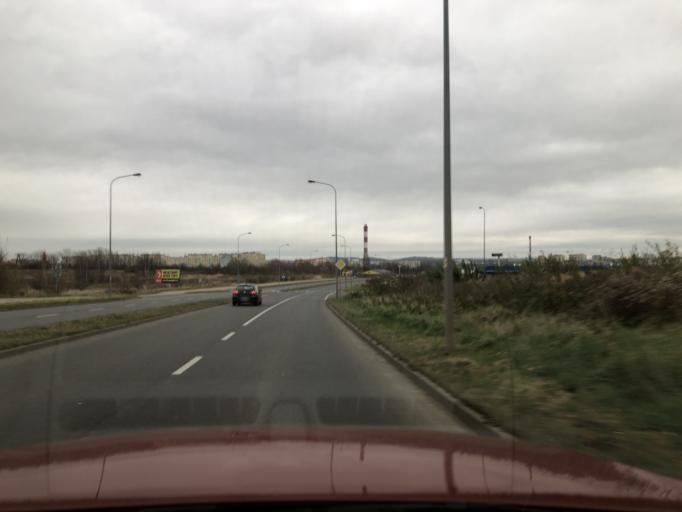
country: PL
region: Lower Silesian Voivodeship
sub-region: Powiat walbrzyski
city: Szczawno-Zdroj
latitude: 50.8192
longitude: 16.2599
